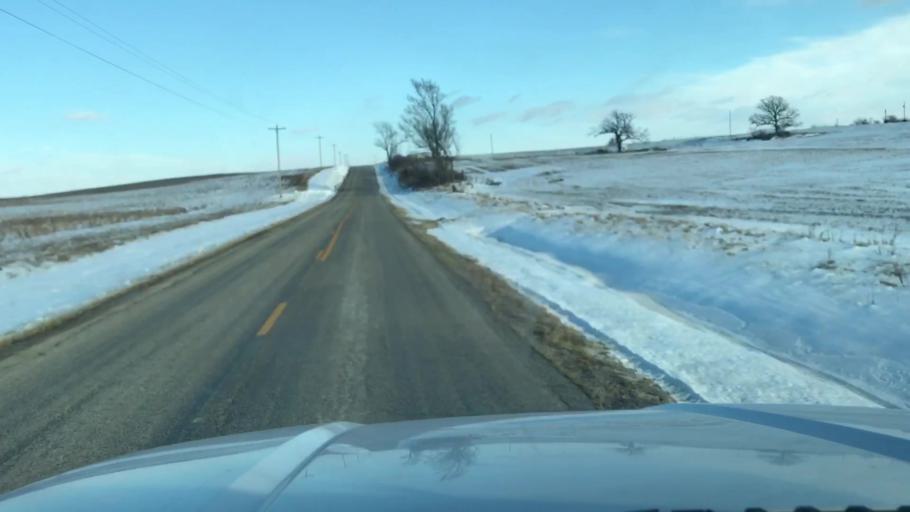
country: US
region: Missouri
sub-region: Holt County
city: Oregon
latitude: 40.1007
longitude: -95.0017
